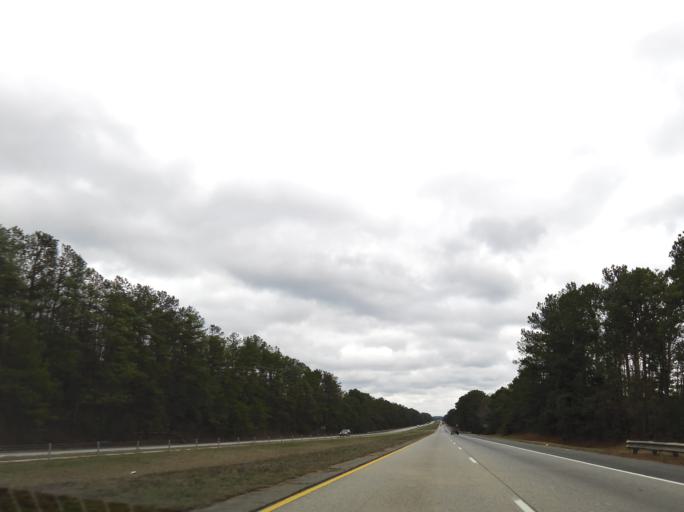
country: US
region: Georgia
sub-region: Bibb County
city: Macon
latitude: 32.7605
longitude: -83.5551
